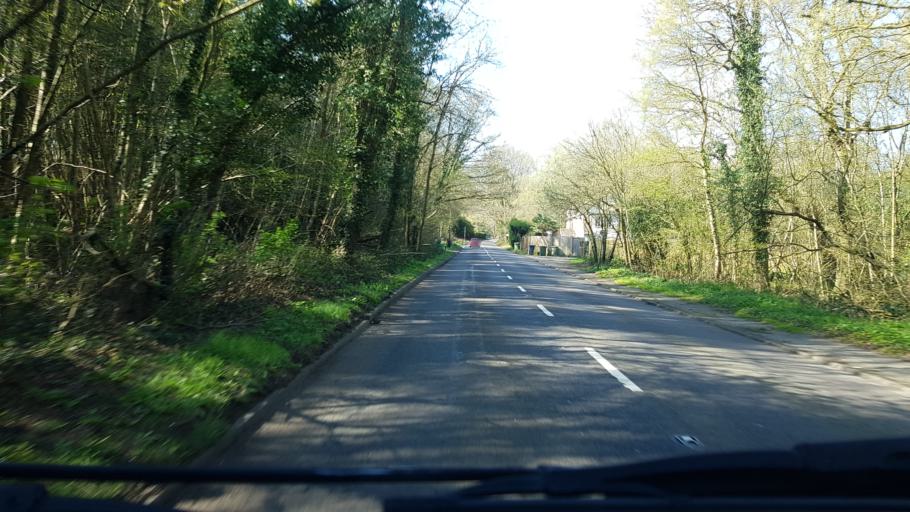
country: GB
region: England
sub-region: Surrey
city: Normandy
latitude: 51.2624
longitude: -0.6783
